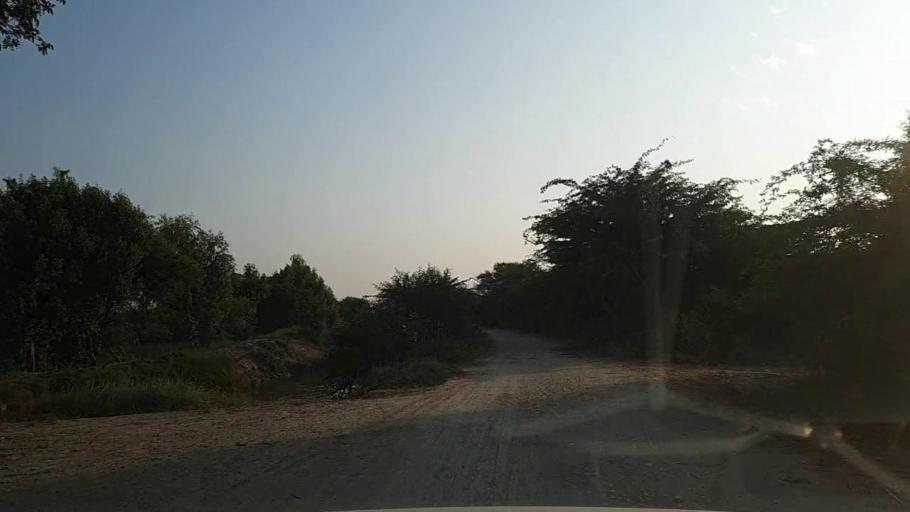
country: PK
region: Sindh
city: Daro Mehar
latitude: 24.7616
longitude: 68.1915
